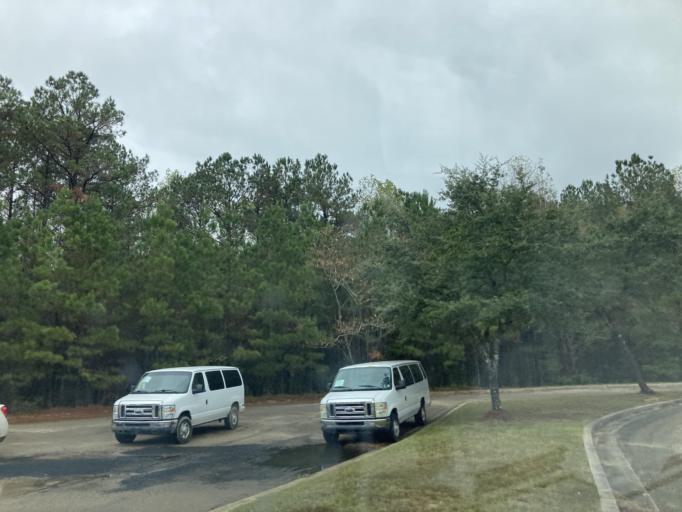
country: US
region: Mississippi
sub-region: Lamar County
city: West Hattiesburg
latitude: 31.2864
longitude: -89.4705
